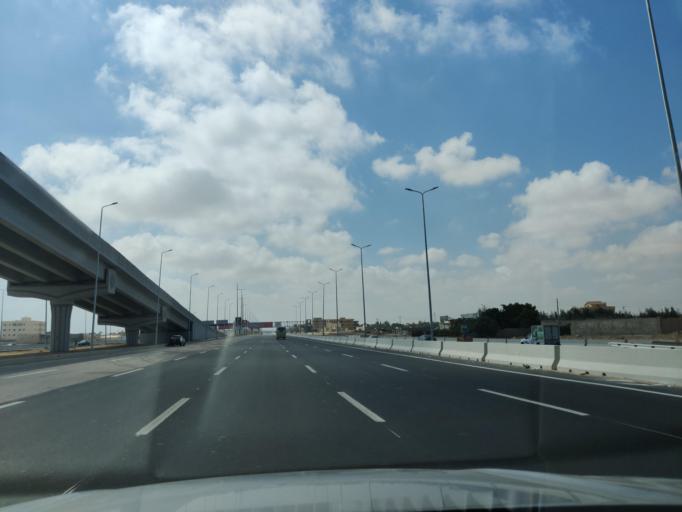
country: EG
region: Muhafazat Matruh
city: Al `Alamayn
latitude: 30.9508
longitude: 28.7720
